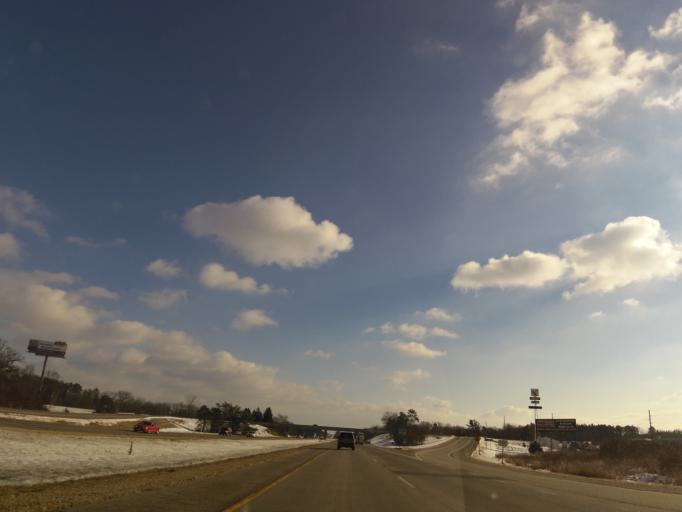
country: US
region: Wisconsin
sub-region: Columbia County
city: Wisconsin Dells
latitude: 43.7193
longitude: -89.8970
